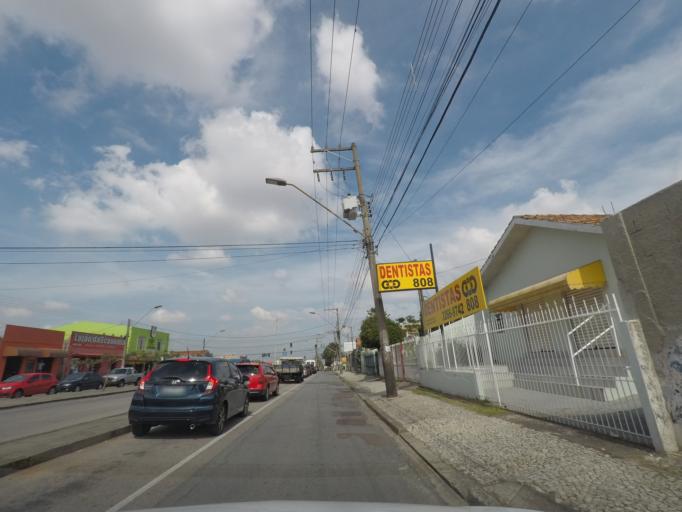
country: BR
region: Parana
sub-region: Pinhais
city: Pinhais
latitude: -25.4535
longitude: -49.2145
